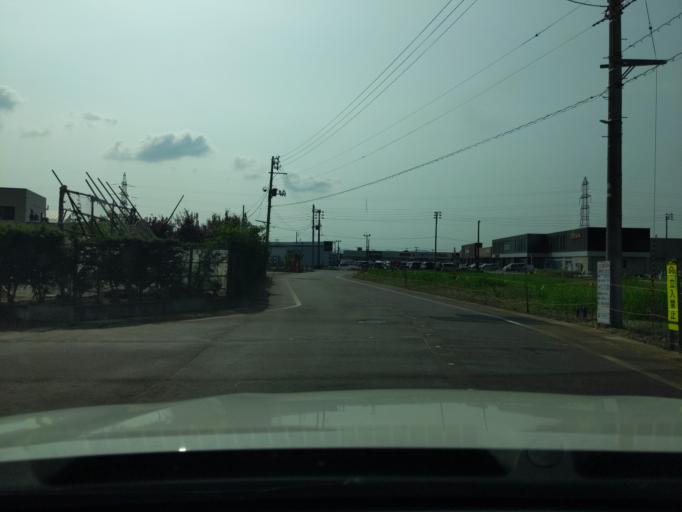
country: JP
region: Niigata
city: Nagaoka
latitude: 37.4290
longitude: 138.8638
